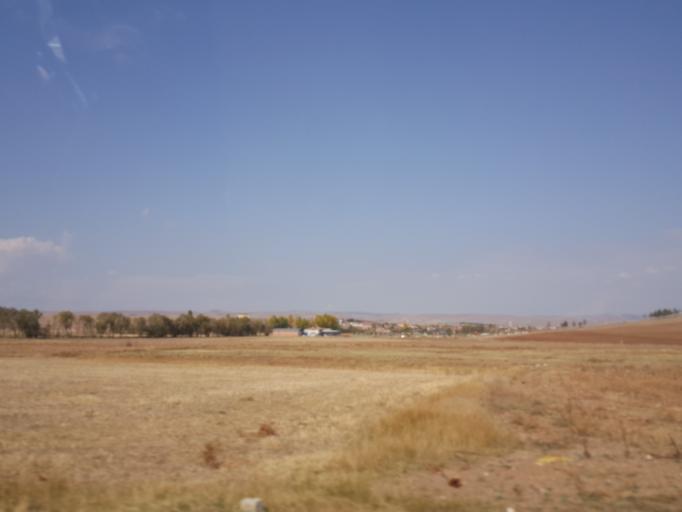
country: TR
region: Corum
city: Alaca
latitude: 40.1465
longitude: 34.8371
